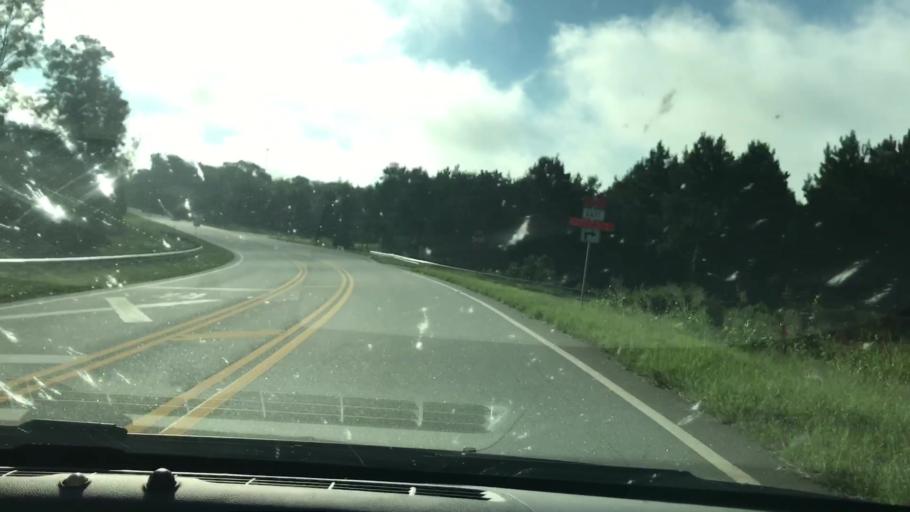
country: US
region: Georgia
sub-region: Terrell County
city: Dawson
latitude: 31.7699
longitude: -84.5013
